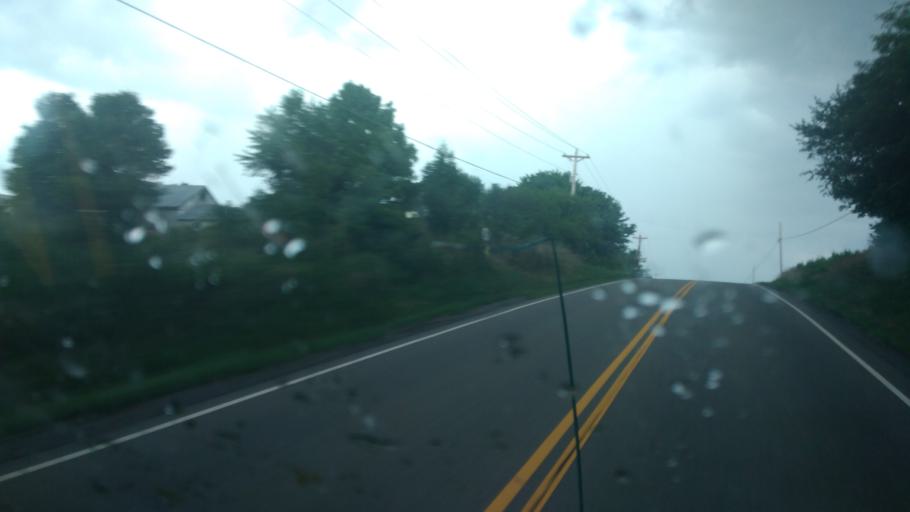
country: US
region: Ohio
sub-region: Licking County
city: Granville
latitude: 40.1579
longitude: -82.5201
